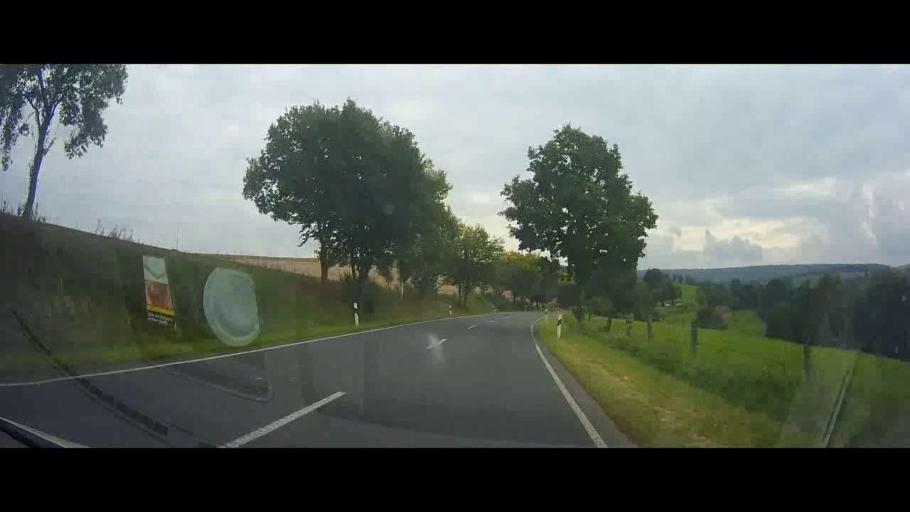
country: DE
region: Lower Saxony
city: Uslar
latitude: 51.6018
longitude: 9.6761
